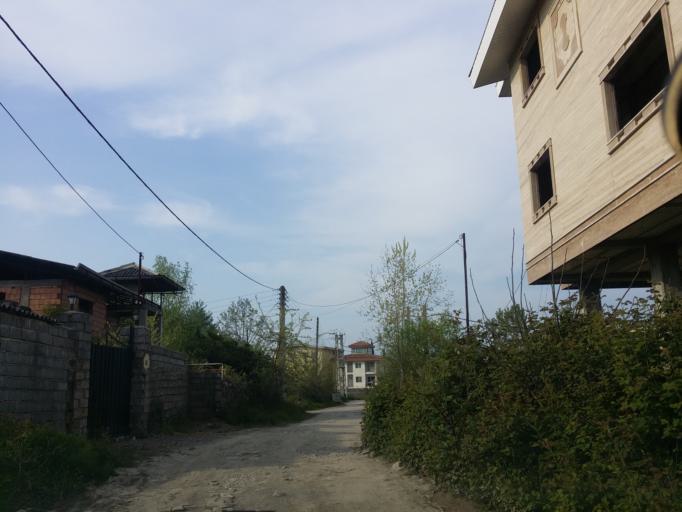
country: IR
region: Mazandaran
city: Chalus
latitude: 36.6822
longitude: 51.3959
